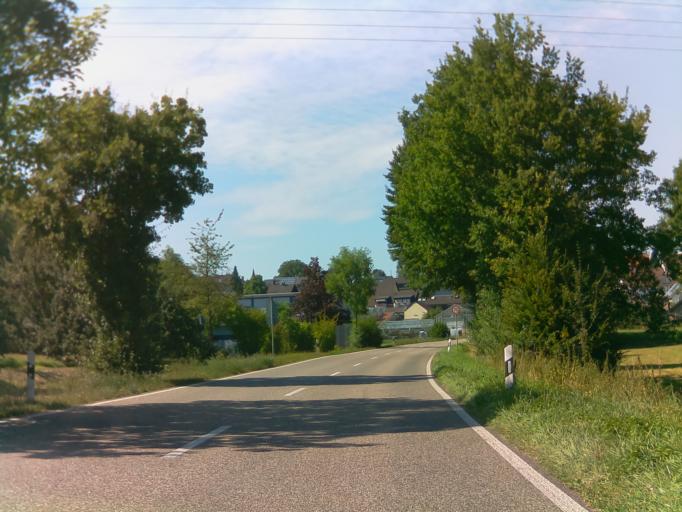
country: DE
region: Baden-Wuerttemberg
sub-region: Karlsruhe Region
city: Oberderdingen
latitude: 49.0987
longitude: 8.7455
